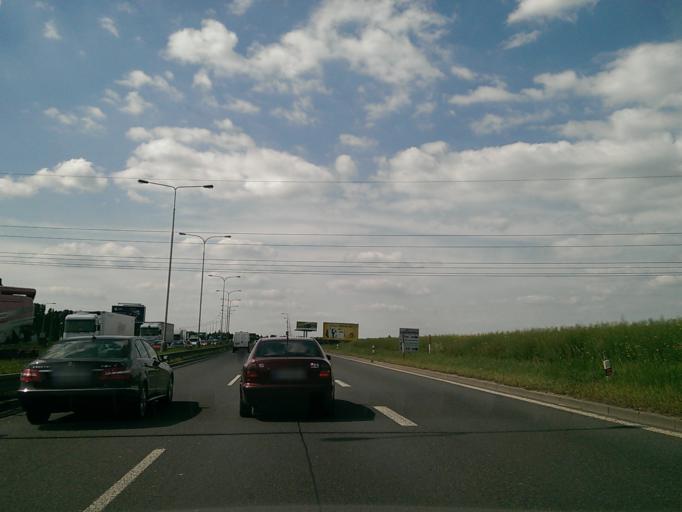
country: CZ
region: Praha
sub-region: Praha 9
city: Strizkov
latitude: 50.1546
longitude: 14.4888
